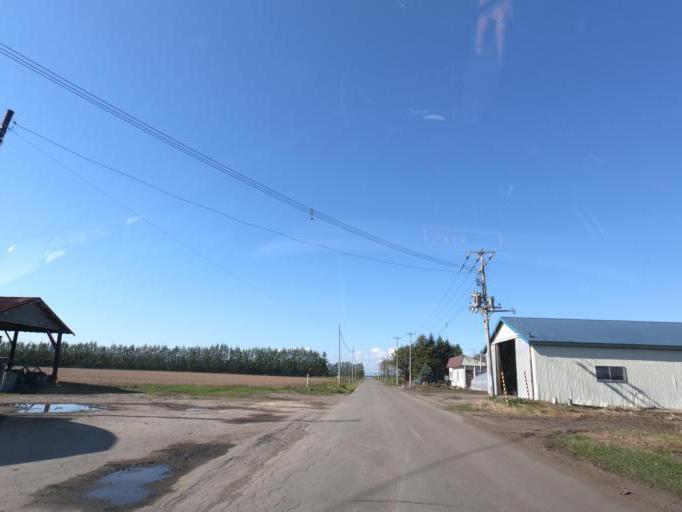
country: JP
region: Hokkaido
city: Otofuke
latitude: 43.0605
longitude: 143.2670
